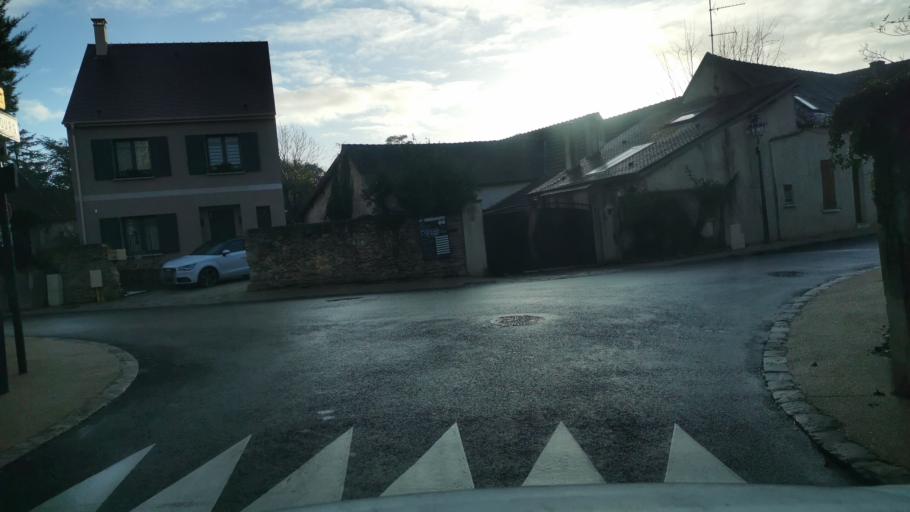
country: FR
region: Ile-de-France
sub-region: Departement des Yvelines
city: Bazainville
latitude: 48.8050
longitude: 1.6666
